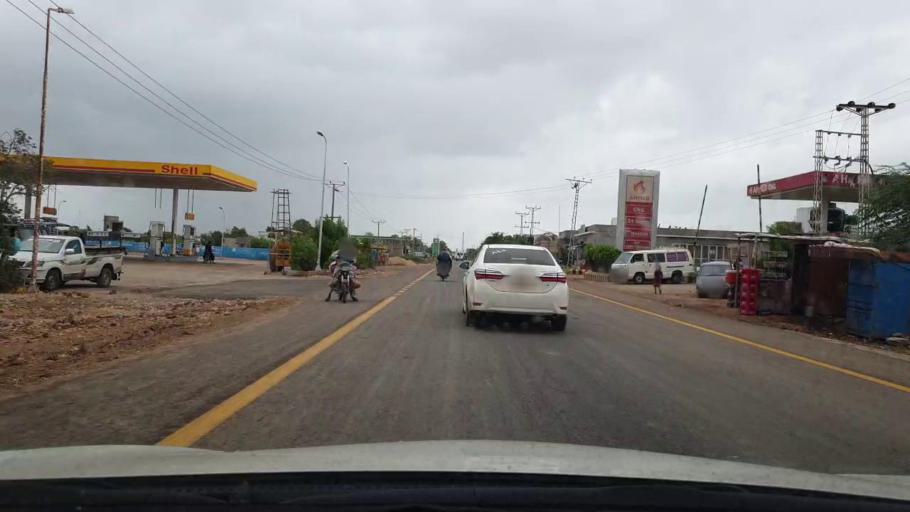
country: PK
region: Sindh
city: Badin
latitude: 24.6557
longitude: 68.8223
